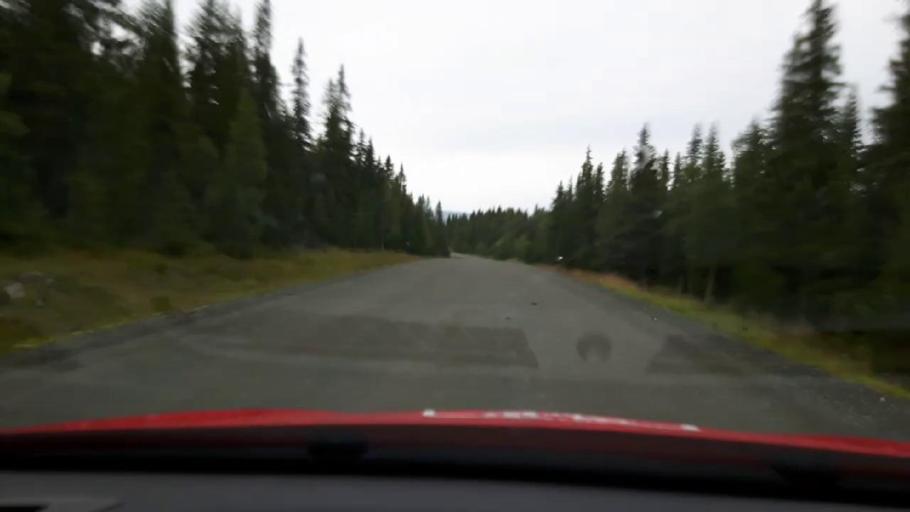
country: SE
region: Jaemtland
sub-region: Are Kommun
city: Are
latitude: 63.4225
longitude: 12.7443
